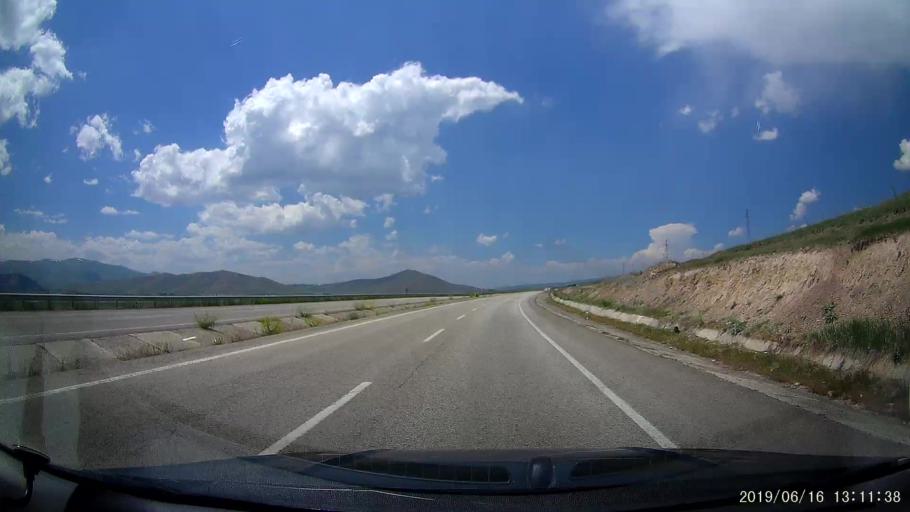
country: TR
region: Agri
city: Diyadin
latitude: 39.5925
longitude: 43.6016
